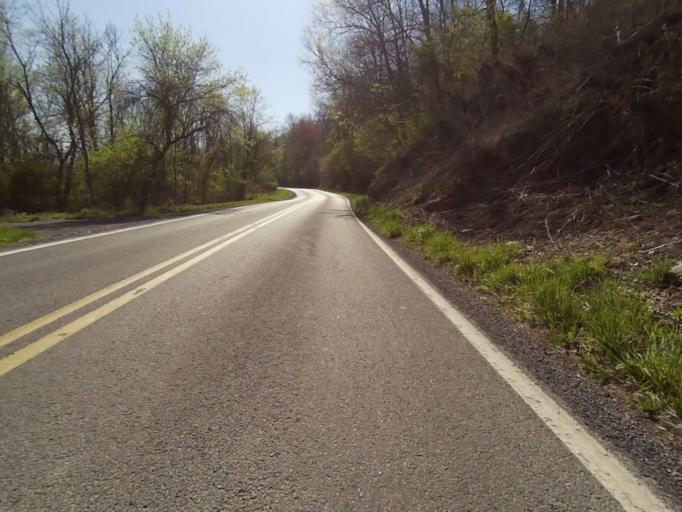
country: US
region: Pennsylvania
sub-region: Centre County
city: Bellefonte
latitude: 40.9072
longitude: -77.7896
